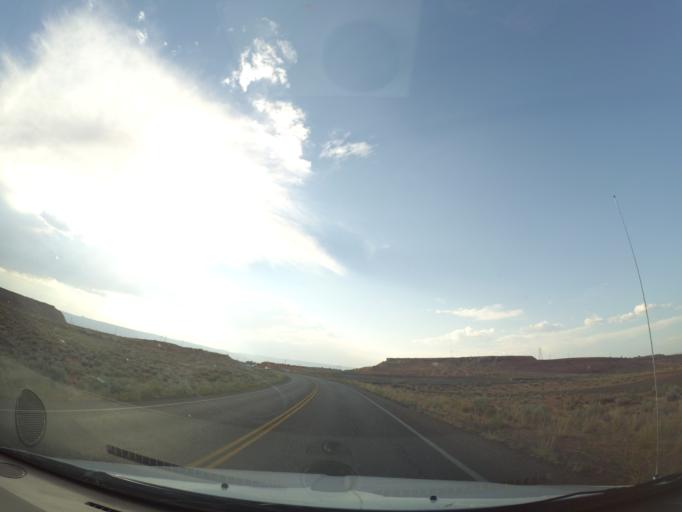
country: US
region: Arizona
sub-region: Coconino County
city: Page
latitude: 36.8975
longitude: -111.4471
